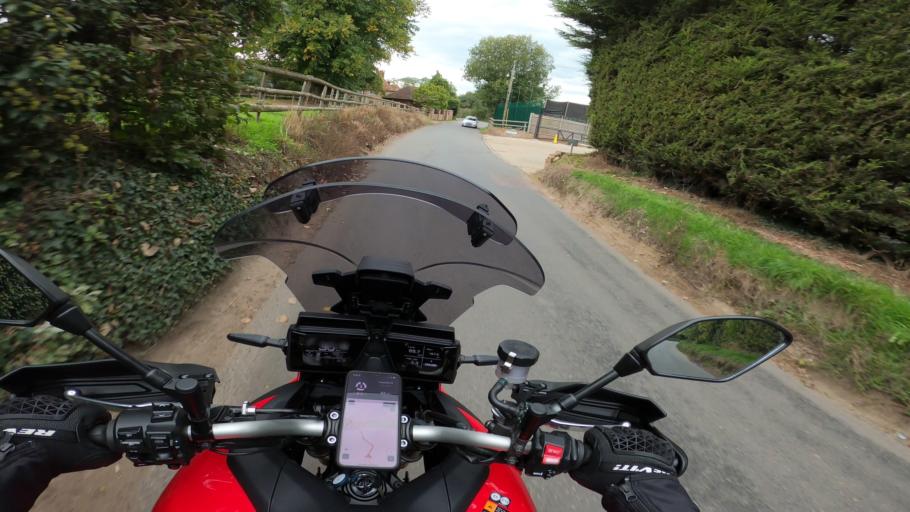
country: GB
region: England
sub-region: Kent
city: Halstead
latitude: 51.3504
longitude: 0.1385
